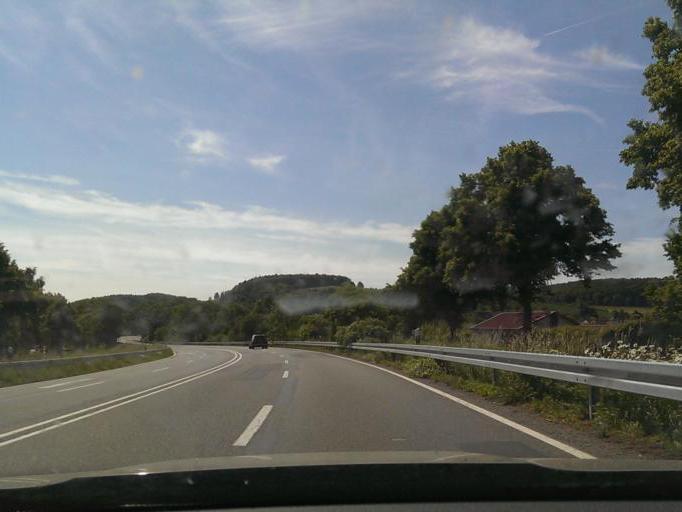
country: DE
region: Lower Saxony
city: Alfeld
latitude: 51.9899
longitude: 9.8001
